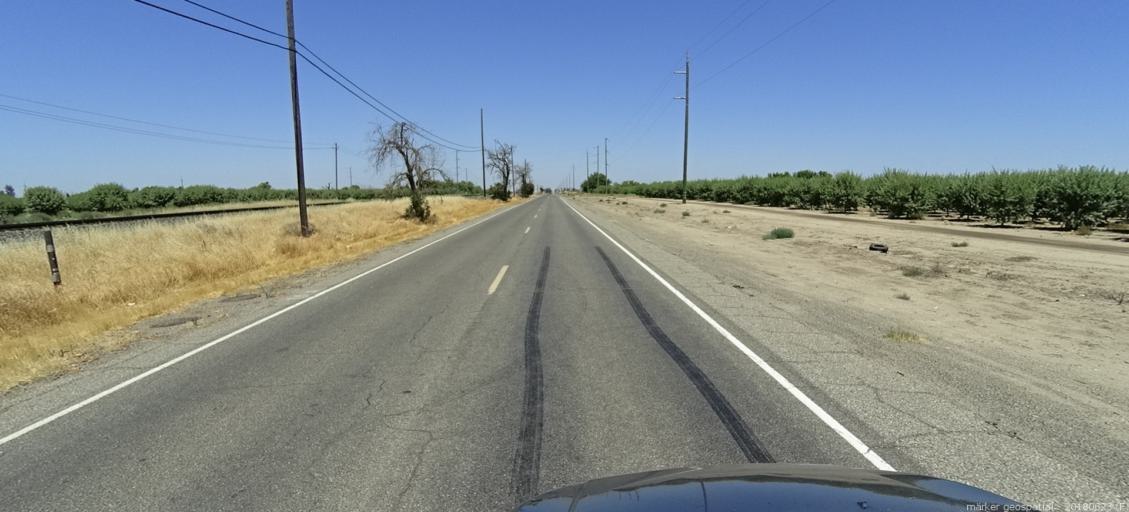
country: US
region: California
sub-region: Madera County
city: Chowchilla
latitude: 37.1041
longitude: -120.2315
